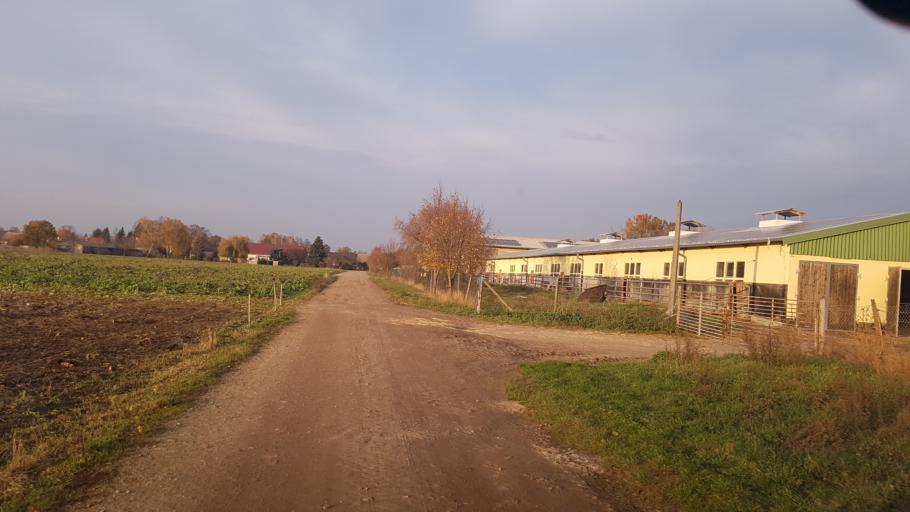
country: DE
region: Brandenburg
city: Schonewalde
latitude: 51.6544
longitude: 13.5986
